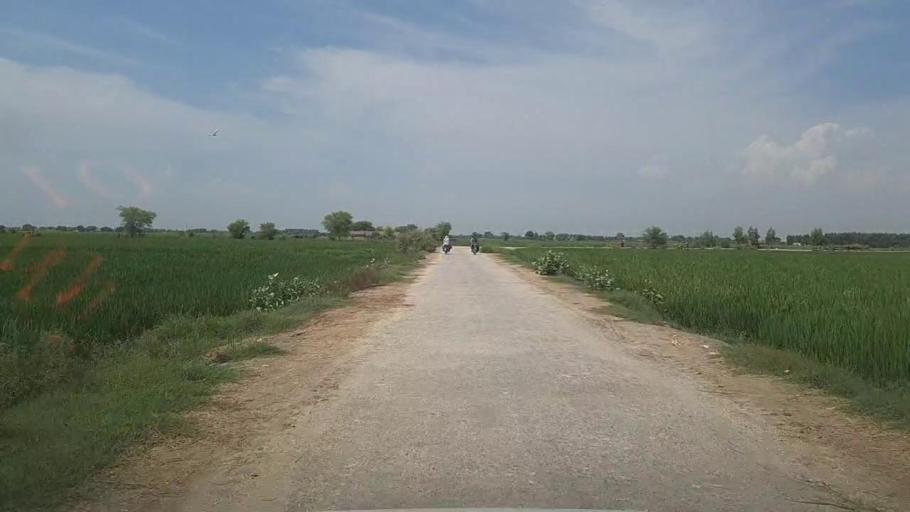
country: PK
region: Sindh
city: Kandhkot
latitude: 28.2850
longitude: 69.2375
